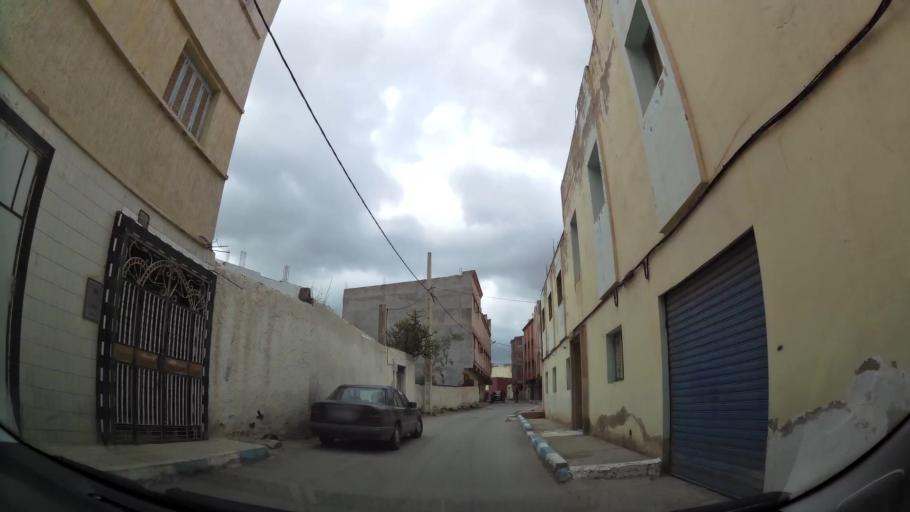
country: MA
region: Oriental
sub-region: Nador
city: Nador
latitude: 35.1650
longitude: -2.9390
